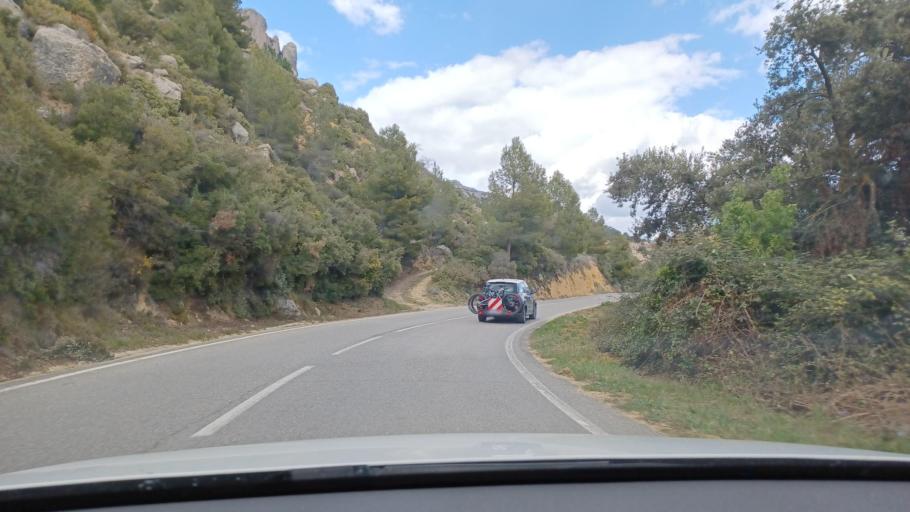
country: ES
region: Catalonia
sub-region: Provincia de Tarragona
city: la Morera de Montsant
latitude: 41.2686
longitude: 0.8482
